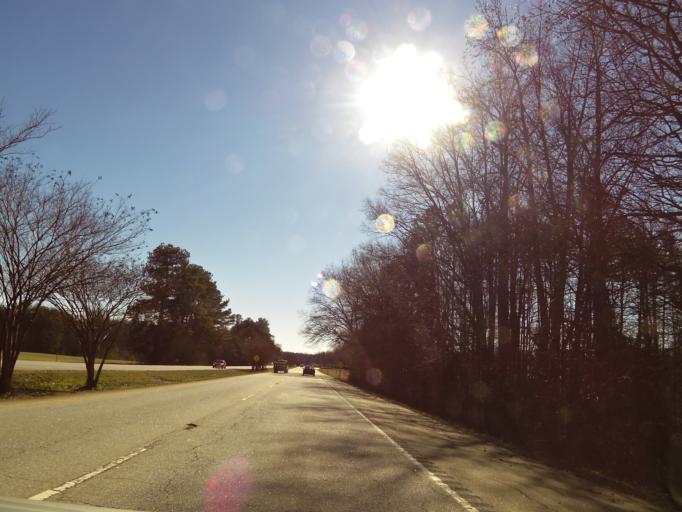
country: US
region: South Carolina
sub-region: Greenville County
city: Travelers Rest
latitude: 34.9295
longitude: -82.4332
